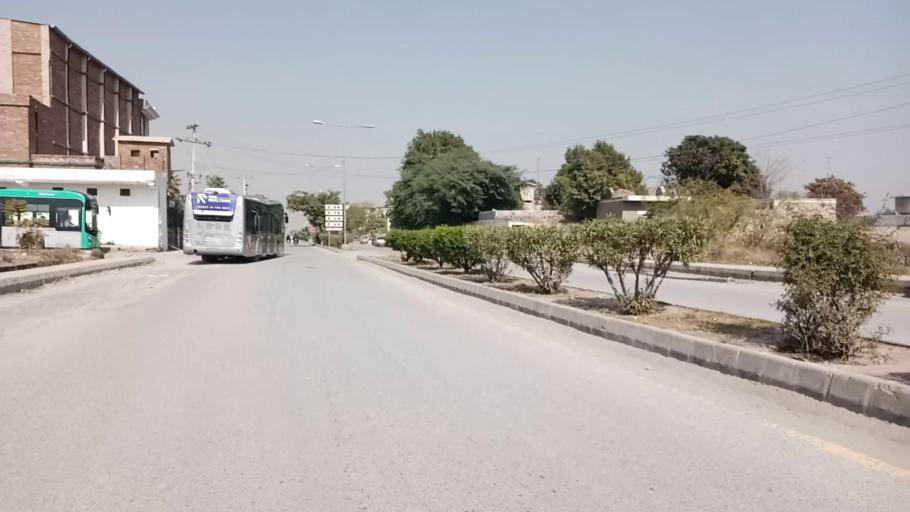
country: PK
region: Khyber Pakhtunkhwa
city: Peshawar
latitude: 33.9569
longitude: 71.4178
